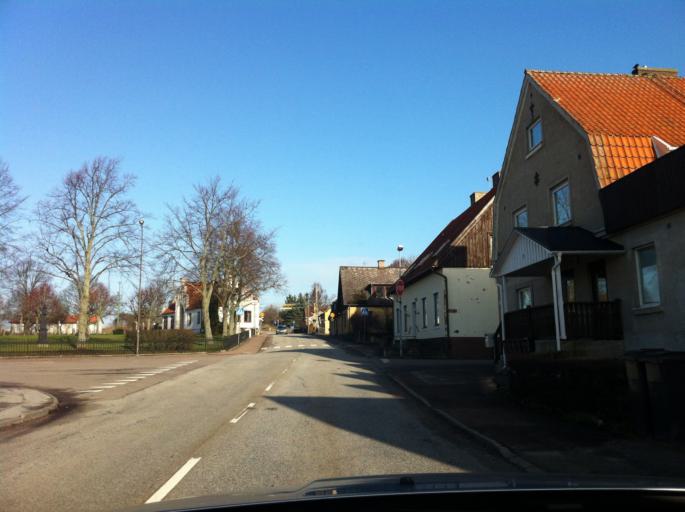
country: SE
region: Skane
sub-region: Landskrona
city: Asmundtorp
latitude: 55.8805
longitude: 13.0002
